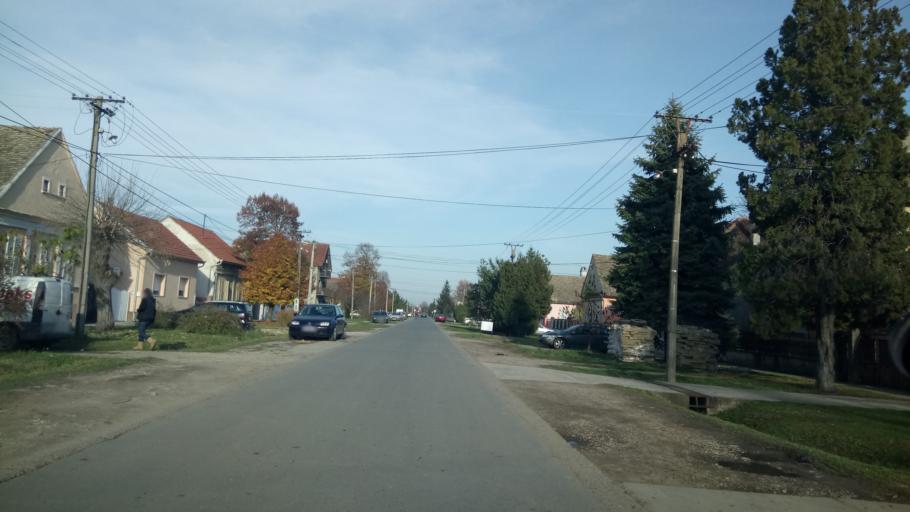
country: RS
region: Autonomna Pokrajina Vojvodina
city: Nova Pazova
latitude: 44.9480
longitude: 20.2237
